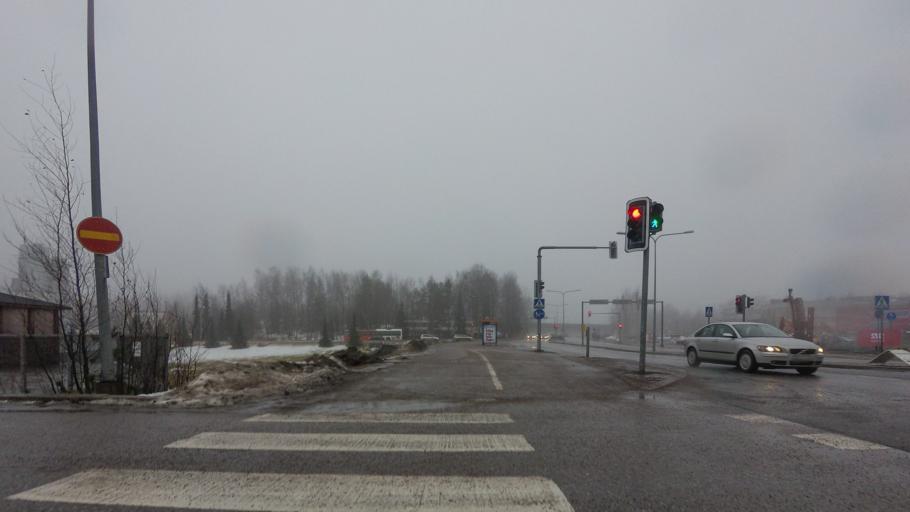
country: FI
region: Uusimaa
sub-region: Helsinki
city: Vantaa
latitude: 60.2105
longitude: 25.0590
